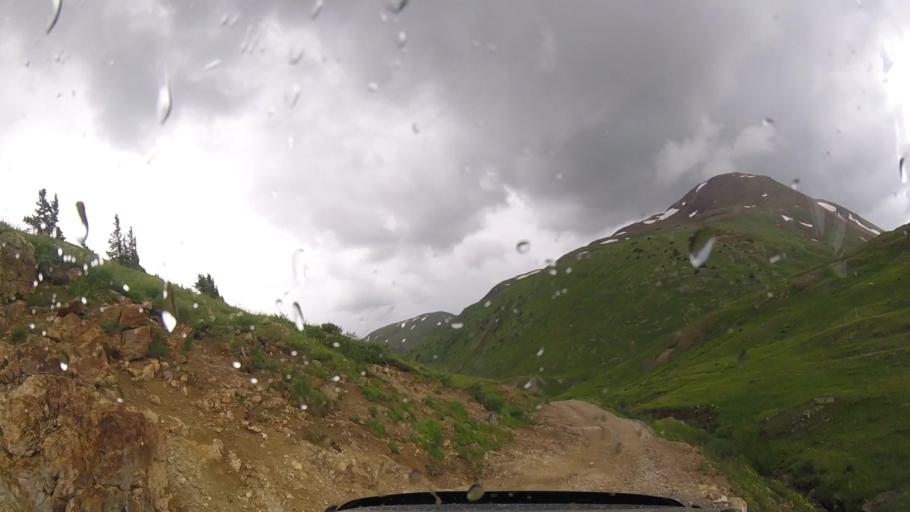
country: US
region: Colorado
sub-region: Ouray County
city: Ouray
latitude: 37.9481
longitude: -107.5737
